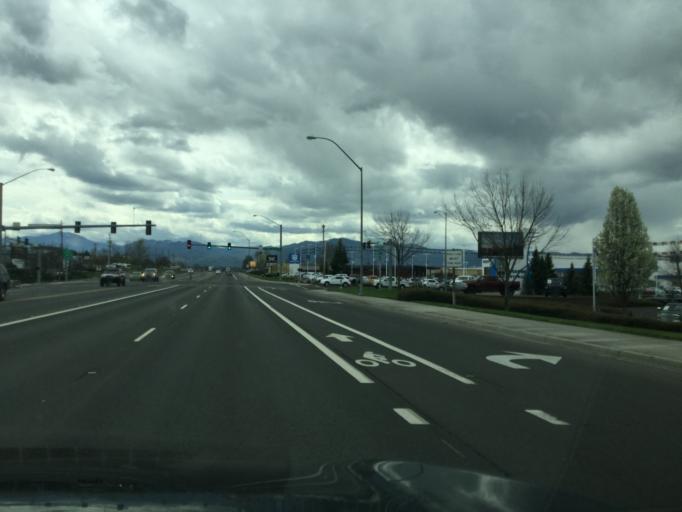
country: US
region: Oregon
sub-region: Jackson County
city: Medford
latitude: 42.3779
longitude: -122.8560
